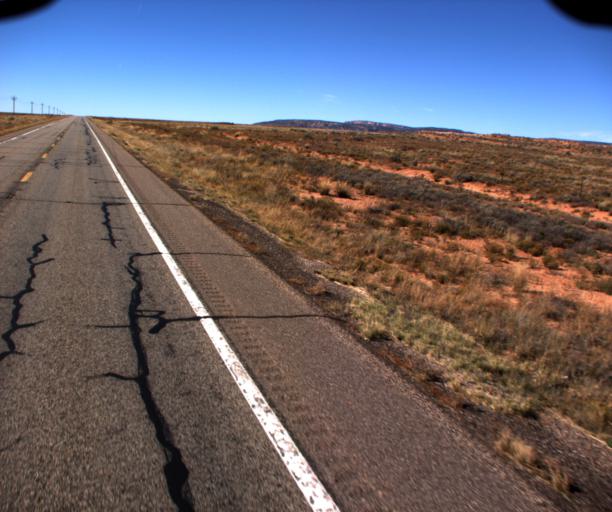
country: US
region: Arizona
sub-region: Coconino County
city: Fredonia
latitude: 36.8920
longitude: -112.6178
